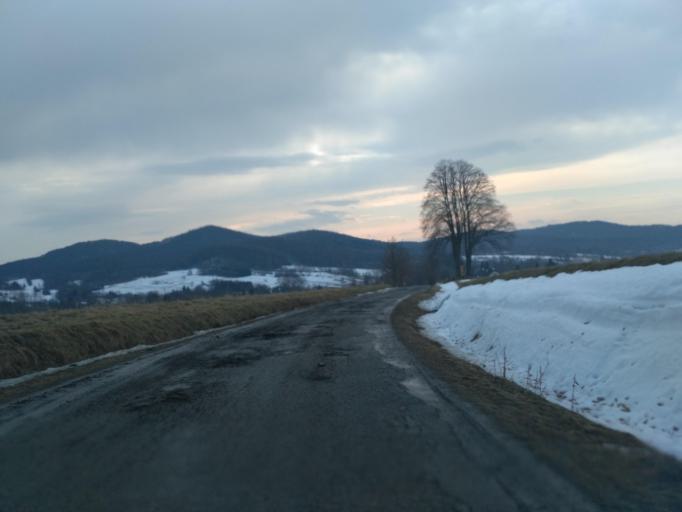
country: PL
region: Subcarpathian Voivodeship
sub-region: Powiat brzozowski
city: Dydnia
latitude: 49.6389
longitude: 22.1643
